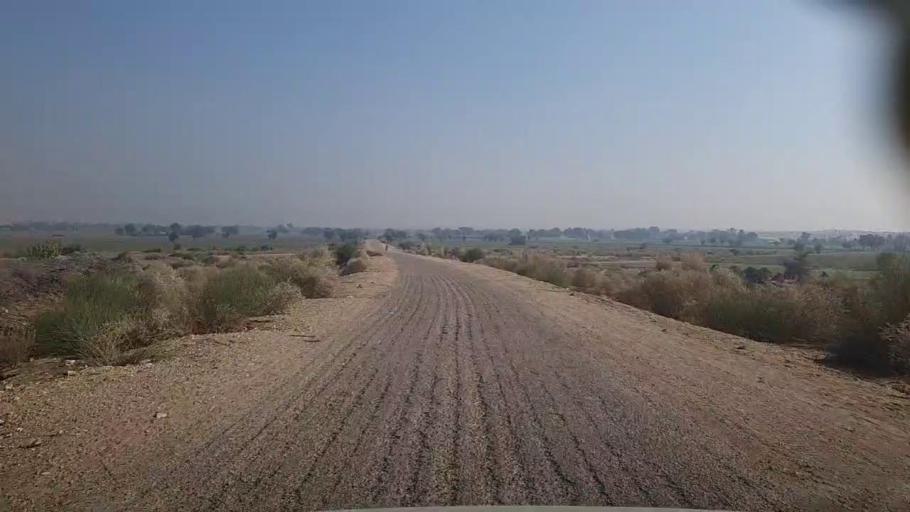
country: PK
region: Sindh
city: Kandiari
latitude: 26.8220
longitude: 68.4906
